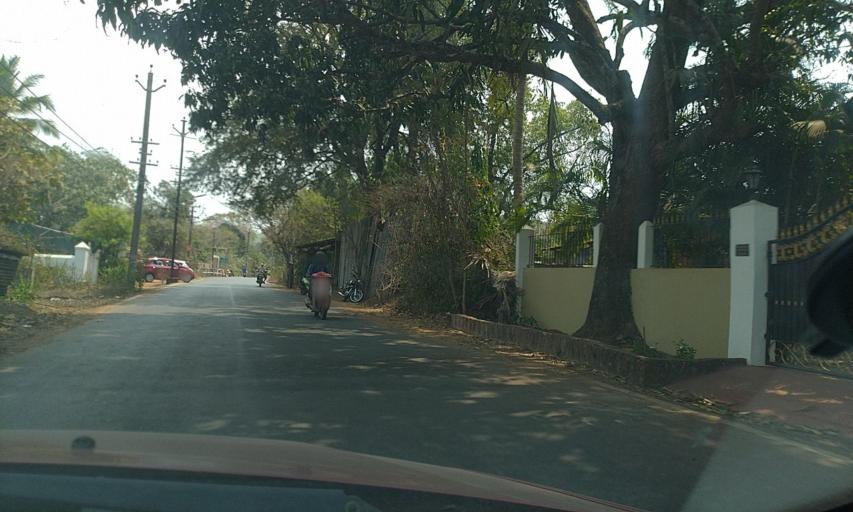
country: IN
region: Goa
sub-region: North Goa
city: Solim
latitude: 15.5909
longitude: 73.7703
